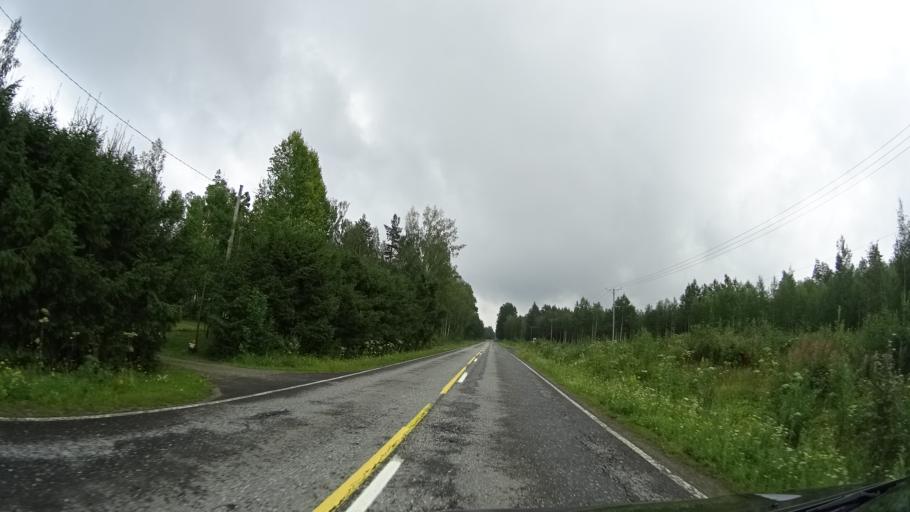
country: FI
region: North Karelia
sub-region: Keski-Karjala
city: Raeaekkylae
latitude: 62.3106
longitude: 29.5225
